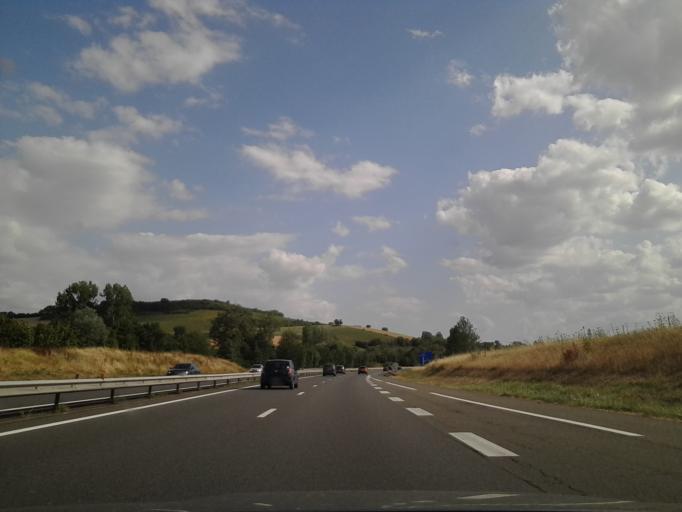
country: FR
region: Auvergne
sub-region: Departement du Puy-de-Dome
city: Combronde
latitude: 45.9914
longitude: 3.1096
